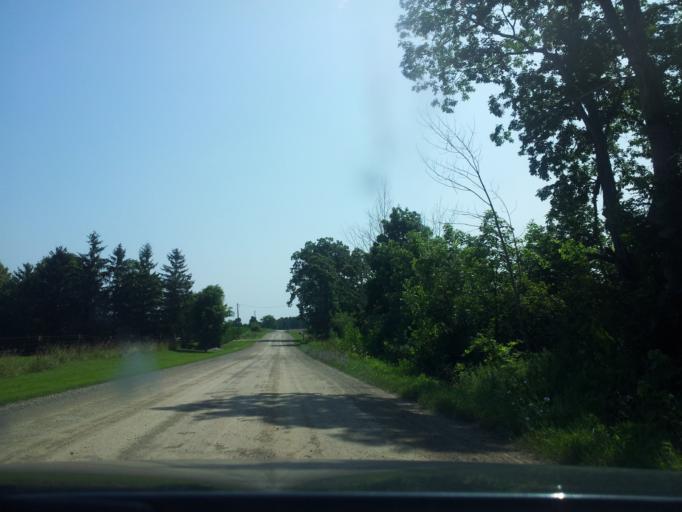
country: CA
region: Ontario
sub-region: Oxford County
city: Woodstock
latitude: 42.9574
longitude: -80.5973
